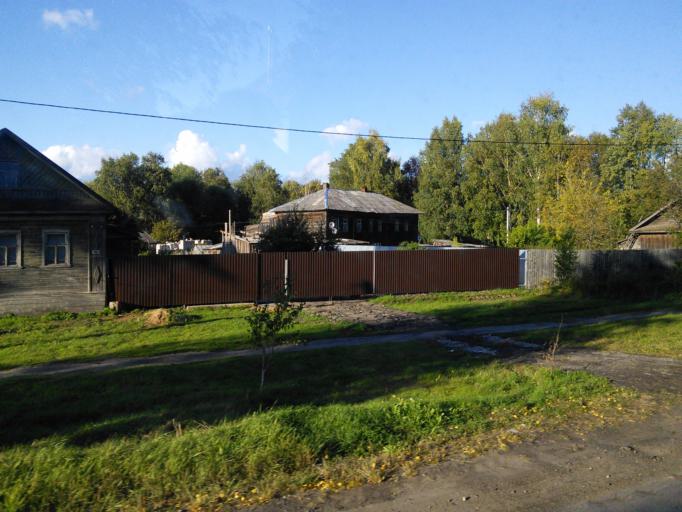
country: RU
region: Jaroslavl
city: Poshekhon'ye
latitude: 58.4976
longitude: 39.1185
